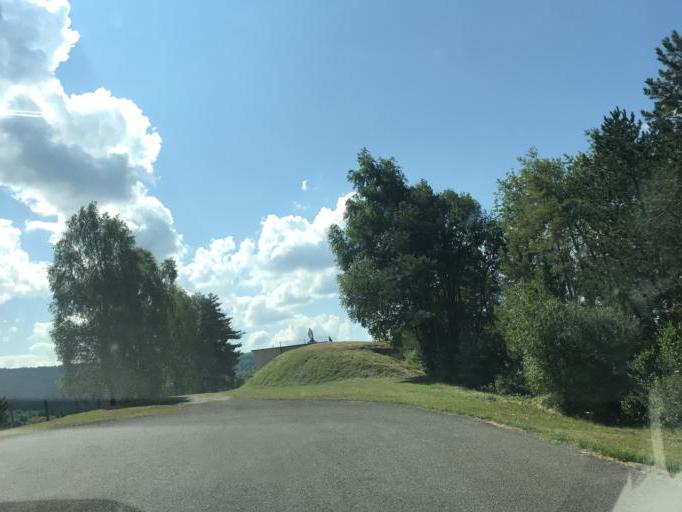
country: FR
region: Franche-Comte
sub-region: Departement du Jura
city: Moirans-en-Montagne
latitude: 46.4617
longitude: 5.7112
